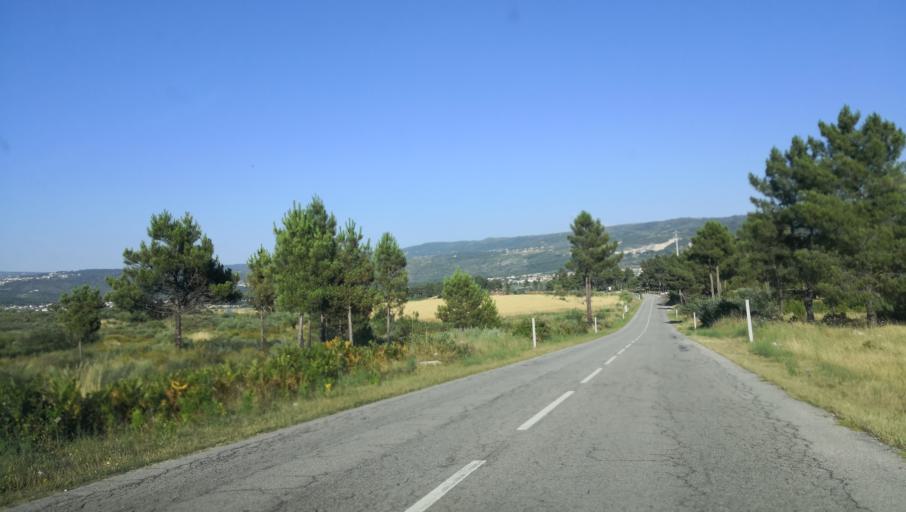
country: PT
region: Vila Real
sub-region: Chaves
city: Chaves
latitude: 41.7687
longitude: -7.4630
